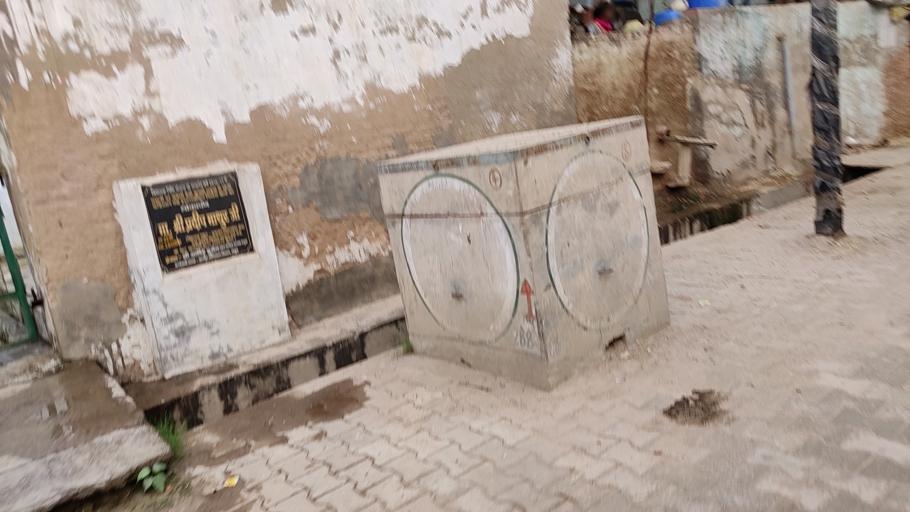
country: IN
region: Uttar Pradesh
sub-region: Mathura
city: Mathura
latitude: 27.5140
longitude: 77.6748
